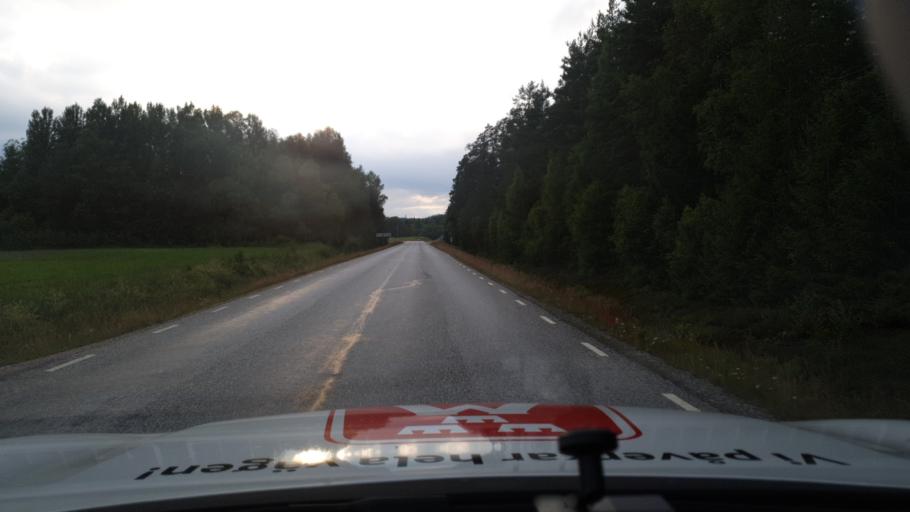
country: SE
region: Dalarna
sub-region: Smedjebackens Kommun
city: Smedjebacken
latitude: 59.9169
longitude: 15.4490
